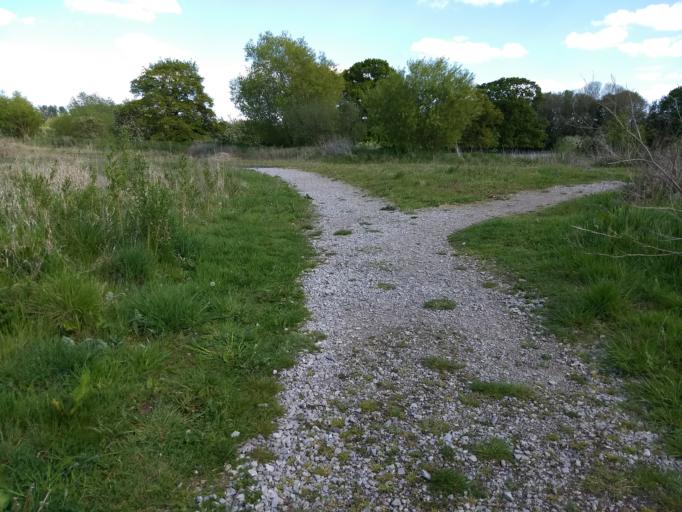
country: GB
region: England
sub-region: Milton Keynes
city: Castlethorpe
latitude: 52.0714
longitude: -0.8190
